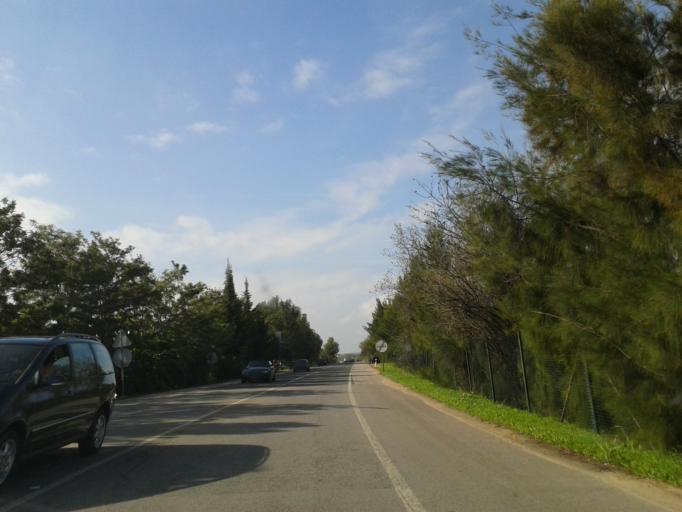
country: PT
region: Faro
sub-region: Tavira
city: Tavira
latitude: 37.1476
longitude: -7.6066
